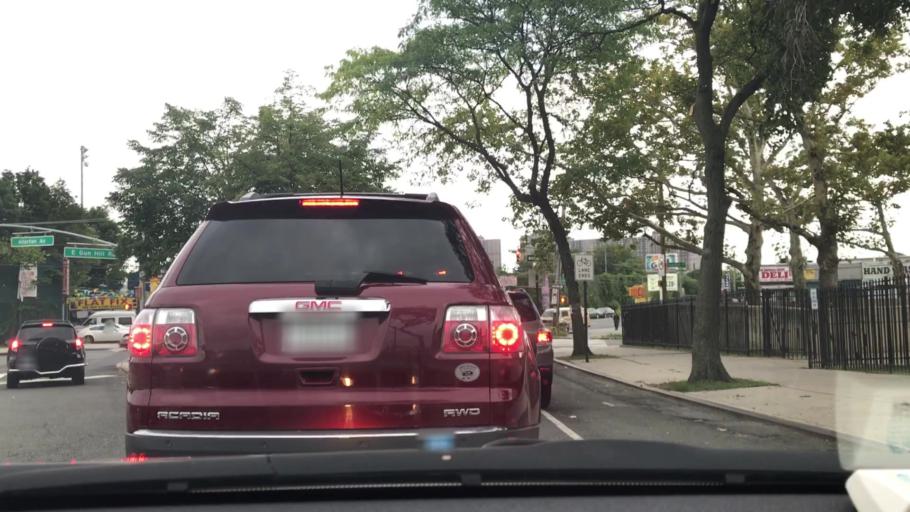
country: US
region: New York
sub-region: Bronx
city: Eastchester
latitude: 40.8651
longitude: -73.8379
